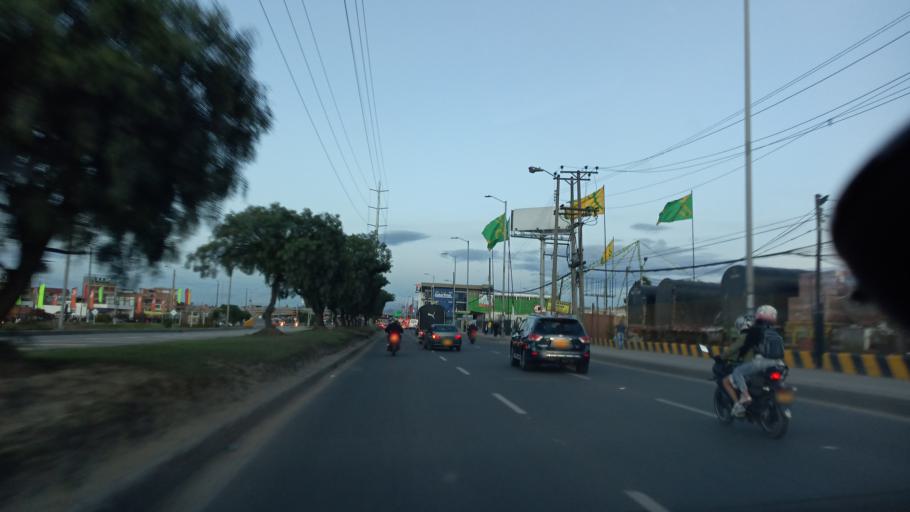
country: CO
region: Cundinamarca
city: Soacha
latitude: 4.5872
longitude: -74.2027
